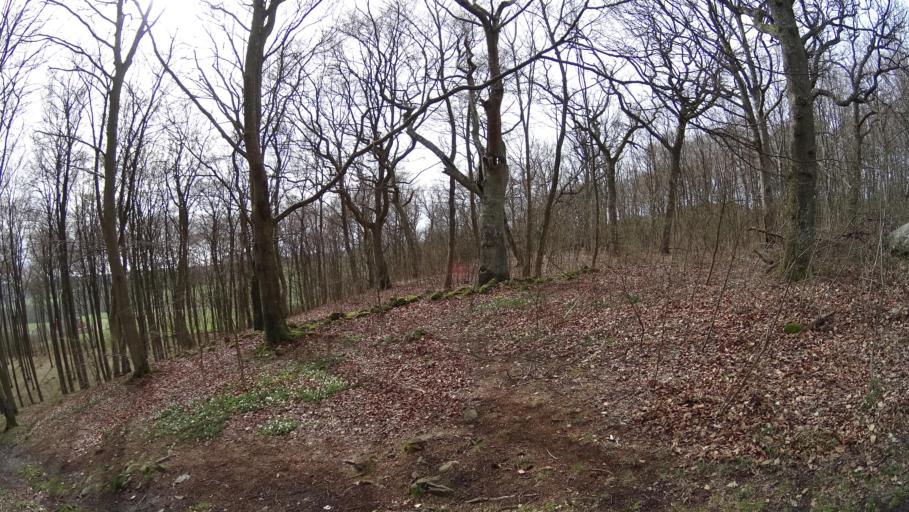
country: SE
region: Skane
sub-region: Hoganas Kommun
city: Hoganas
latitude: 56.2794
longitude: 12.5419
